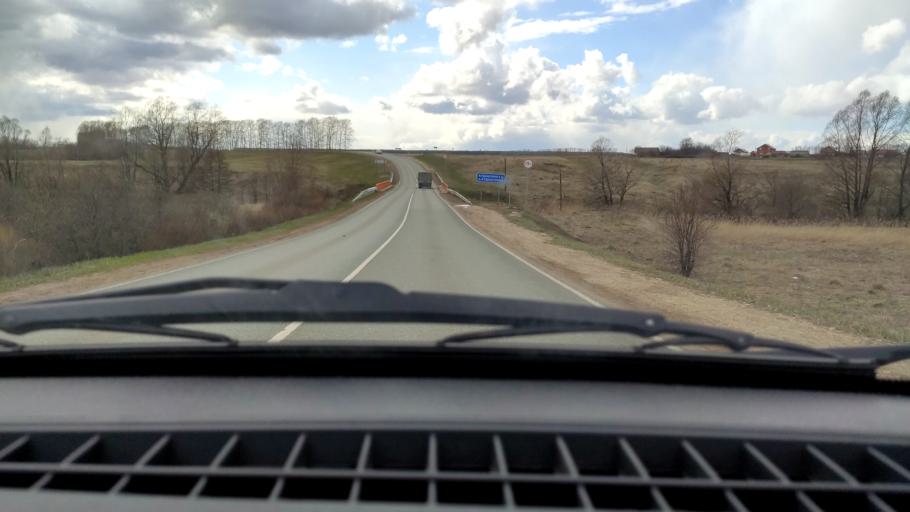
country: RU
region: Bashkortostan
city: Kushnarenkovo
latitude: 55.0666
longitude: 55.2525
